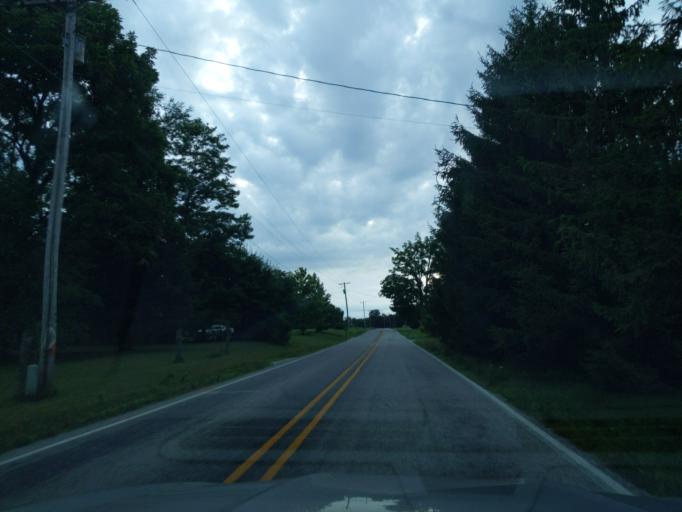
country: US
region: Indiana
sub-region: Ripley County
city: Osgood
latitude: 39.1948
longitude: -85.2629
